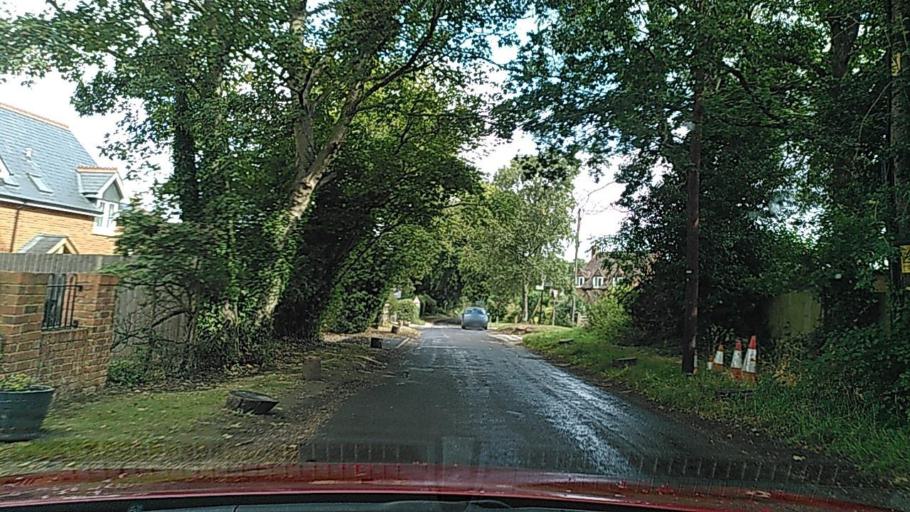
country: GB
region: England
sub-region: Wokingham
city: Sonning
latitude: 51.5073
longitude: -0.9302
